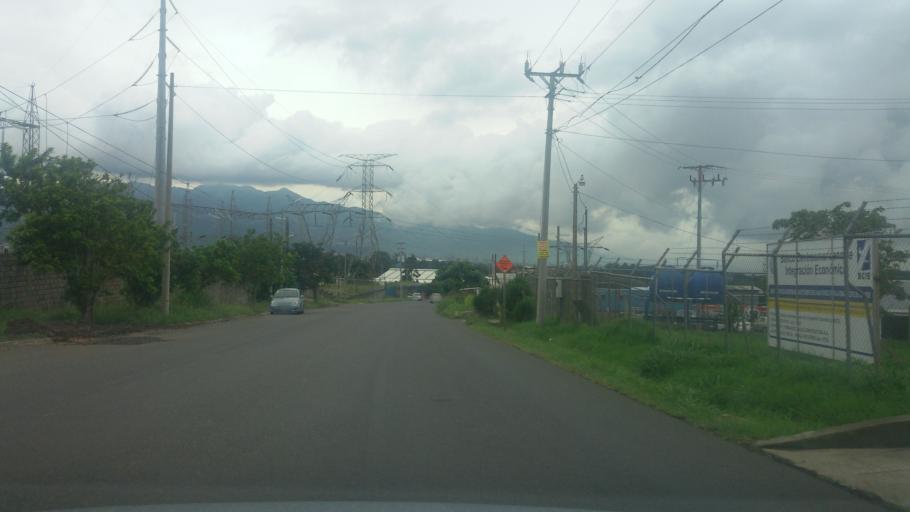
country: CR
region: Heredia
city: Angeles
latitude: 9.9817
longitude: -84.0548
